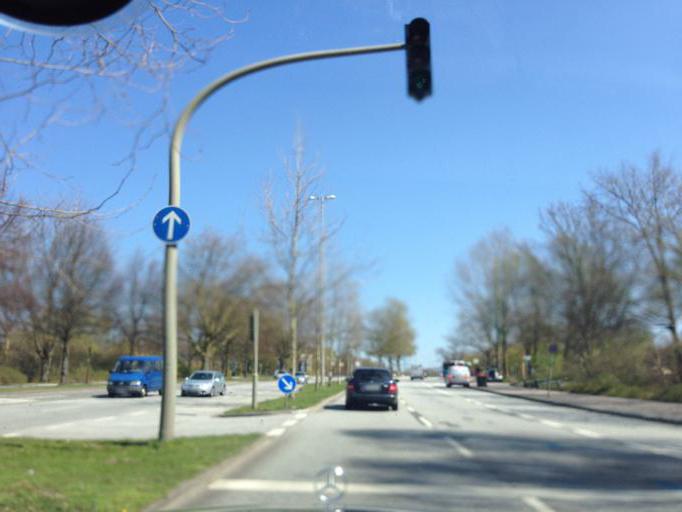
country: DE
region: Hamburg
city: Barmbek-Nord
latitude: 53.6067
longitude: 10.0295
